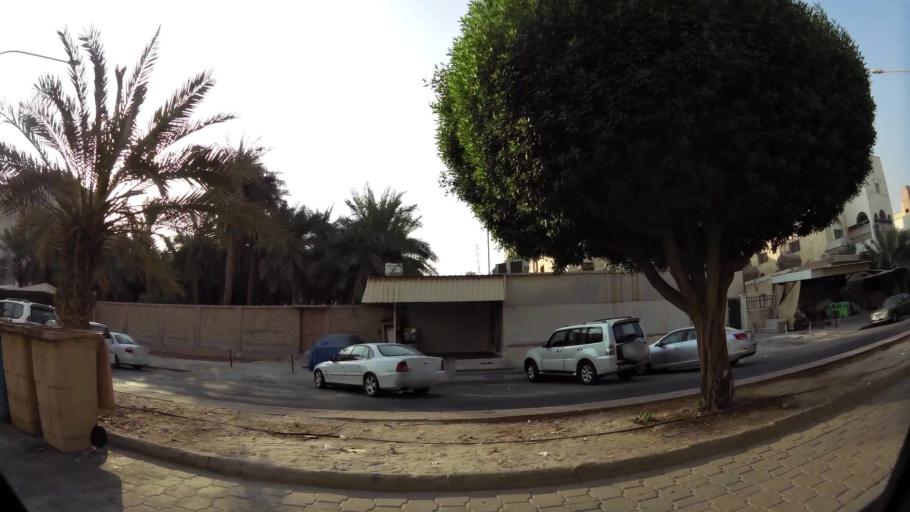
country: KW
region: Muhafazat Hawalli
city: Salwa
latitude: 29.3030
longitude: 48.0746
